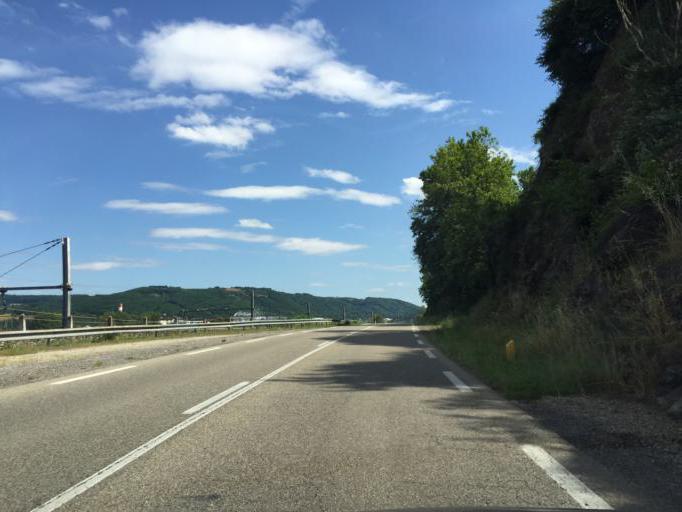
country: FR
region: Rhone-Alpes
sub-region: Departement de l'Ardeche
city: Andance
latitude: 45.2242
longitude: 4.8023
